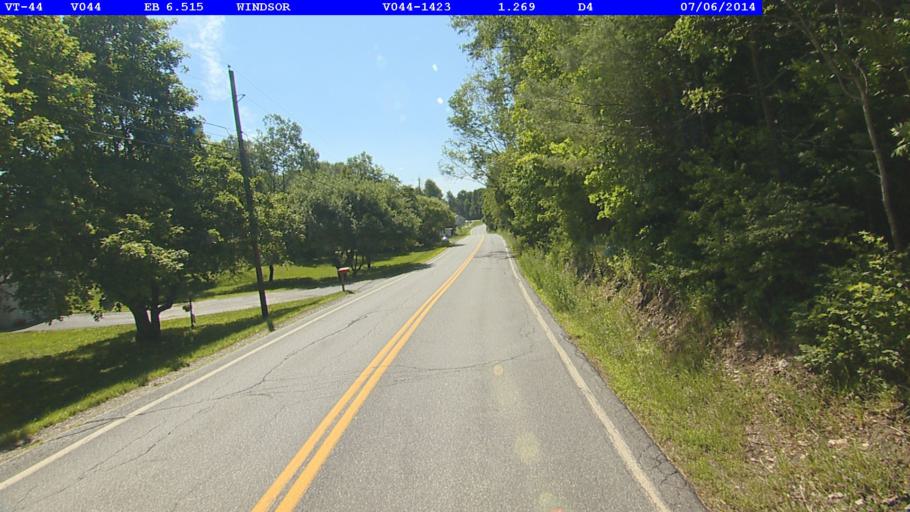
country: US
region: Vermont
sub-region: Windsor County
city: Windsor
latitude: 43.4625
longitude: -72.4292
